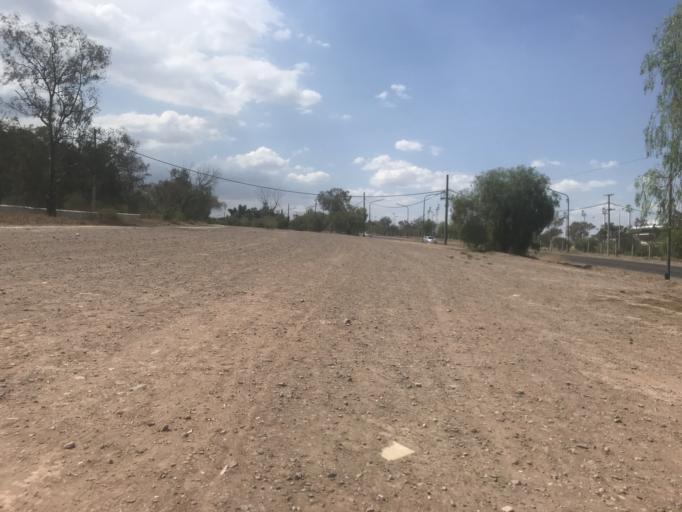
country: AR
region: Mendoza
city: Mendoza
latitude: -32.8880
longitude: -68.8847
